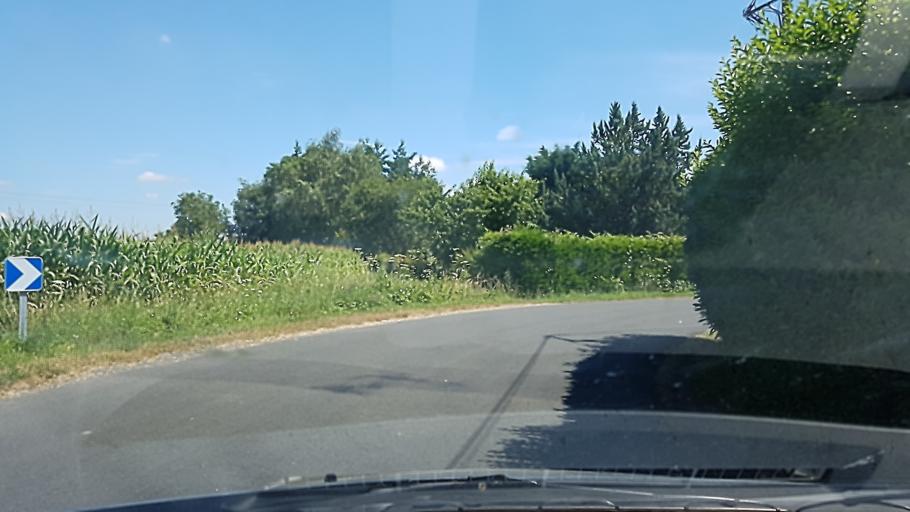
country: FR
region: Pays de la Loire
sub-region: Departement de Maine-et-Loire
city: Le Plessis-Grammoire
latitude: 47.5109
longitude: -0.4114
